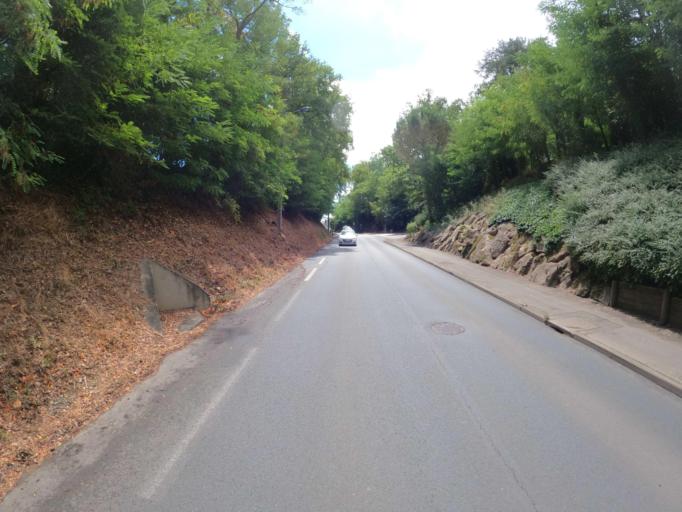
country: FR
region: Pays de la Loire
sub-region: Departement de Maine-et-Loire
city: Avrille
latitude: 47.5316
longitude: -0.6141
